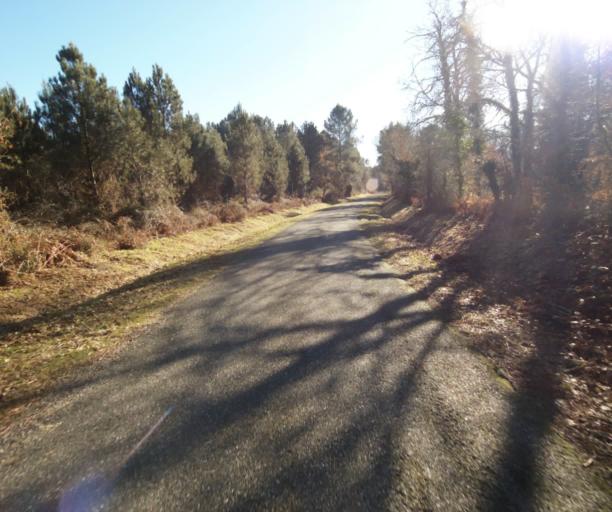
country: FR
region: Aquitaine
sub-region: Departement des Landes
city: Gabarret
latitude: 44.0986
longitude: 0.0886
